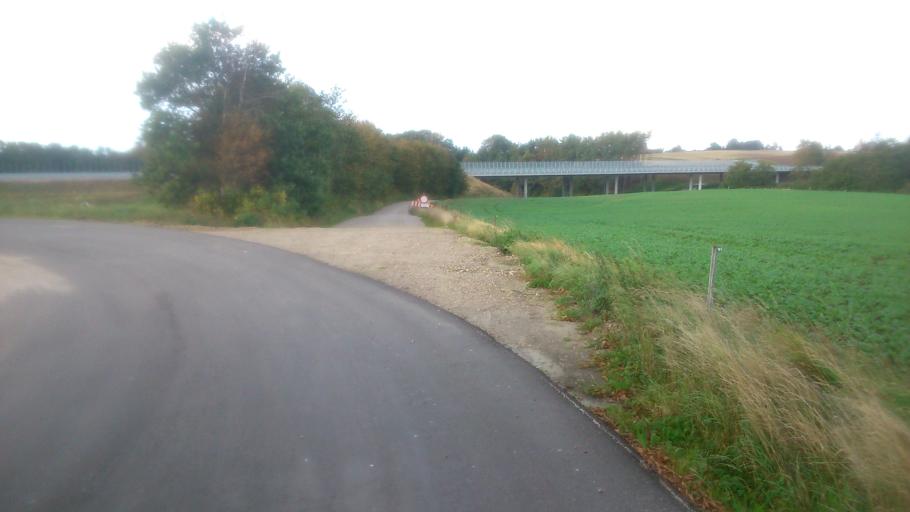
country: DK
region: Central Jutland
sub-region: Silkeborg Kommune
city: Silkeborg
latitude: 56.2008
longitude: 9.5184
